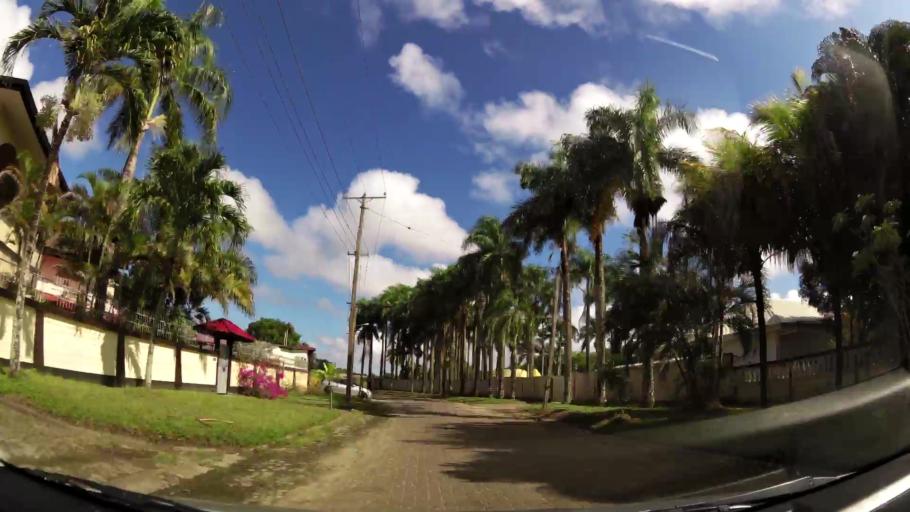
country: SR
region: Commewijne
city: Nieuw Amsterdam
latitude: 5.8736
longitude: -55.1028
